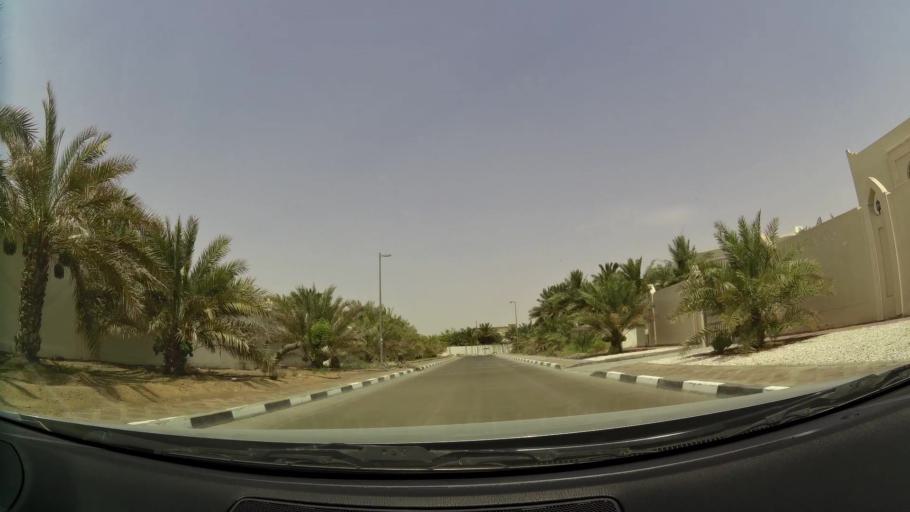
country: AE
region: Abu Dhabi
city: Al Ain
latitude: 24.2006
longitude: 55.7434
